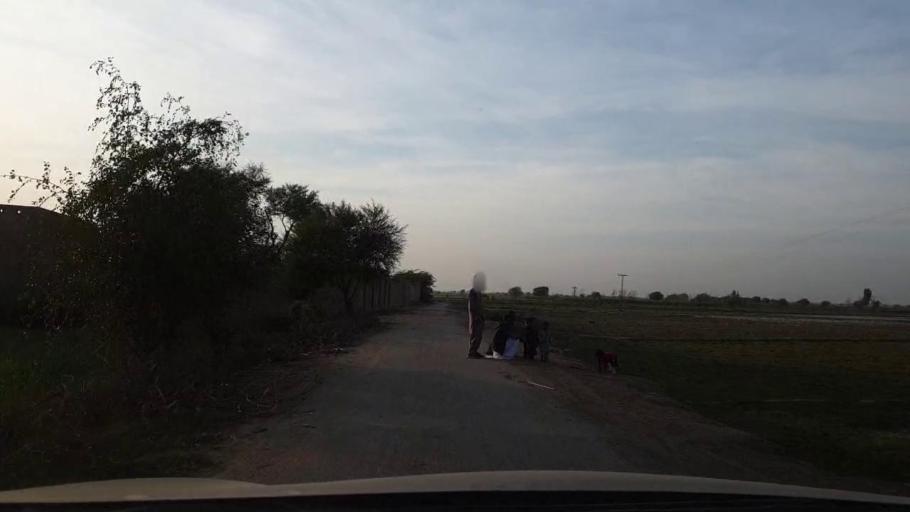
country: PK
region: Sindh
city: Tando Adam
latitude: 25.7151
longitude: 68.7244
